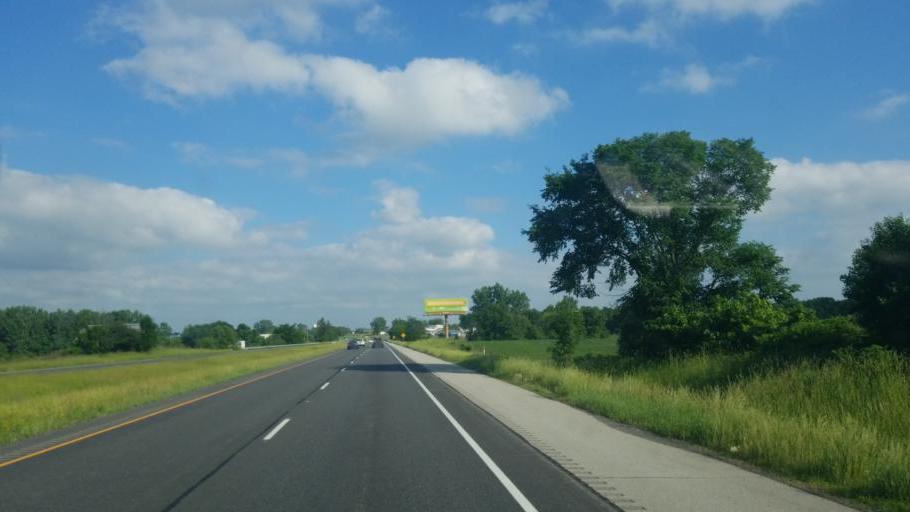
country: US
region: Indiana
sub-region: Whitley County
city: Columbia City
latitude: 41.1518
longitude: -85.4543
